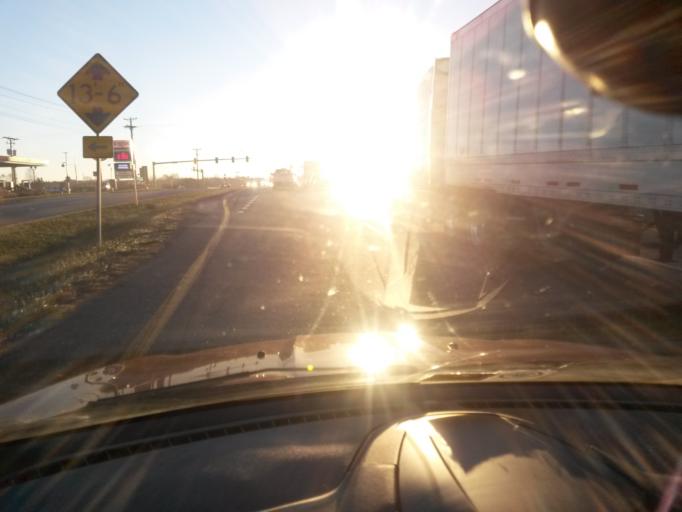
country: US
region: Virginia
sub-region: Franklin County
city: Rocky Mount
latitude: 37.0720
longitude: -79.8991
